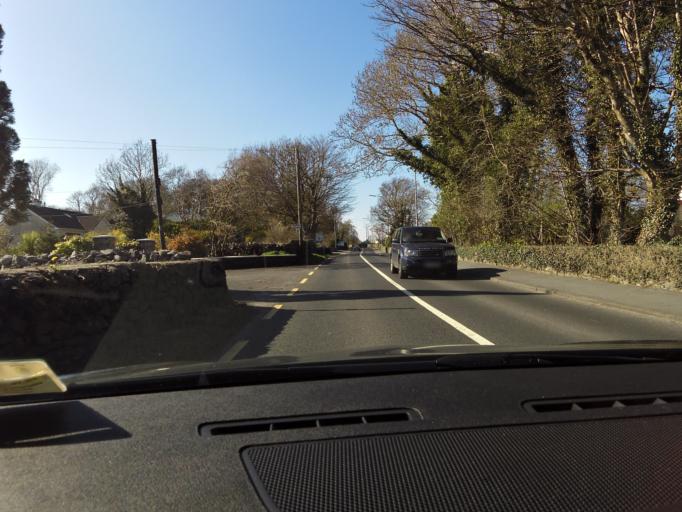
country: IE
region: Connaught
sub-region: County Galway
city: Oughterard
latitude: 53.4251
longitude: -9.3117
